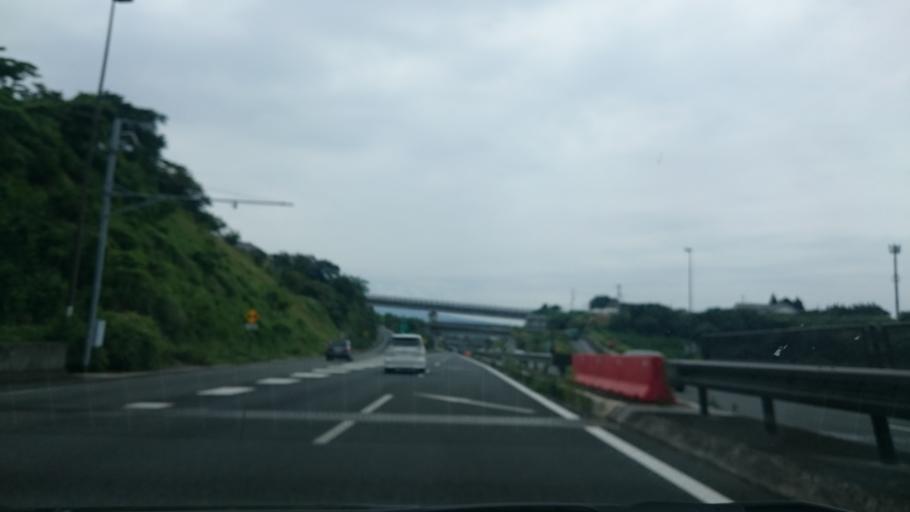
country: JP
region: Shizuoka
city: Mishima
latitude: 35.1343
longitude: 138.9408
